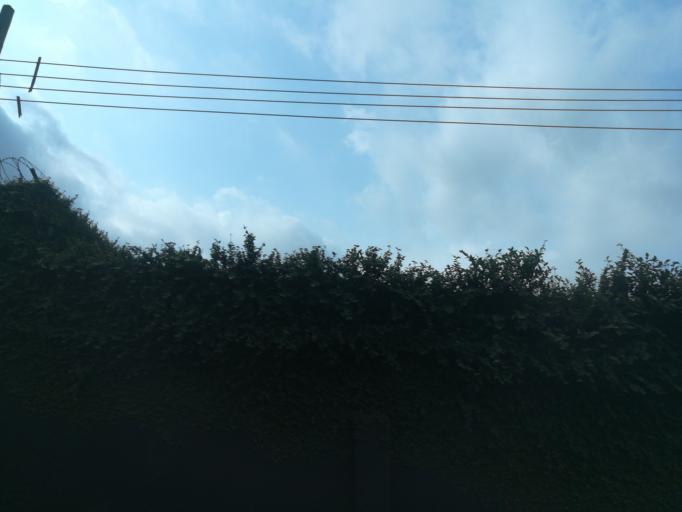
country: NG
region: Lagos
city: Oshodi
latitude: 6.5726
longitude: 3.3588
